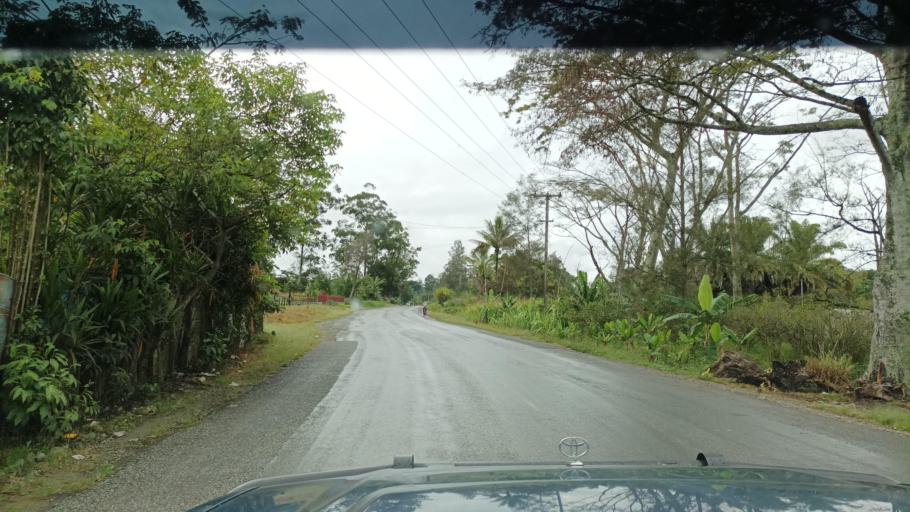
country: PG
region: Jiwaka
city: Minj
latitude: -5.8545
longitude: 144.6293
